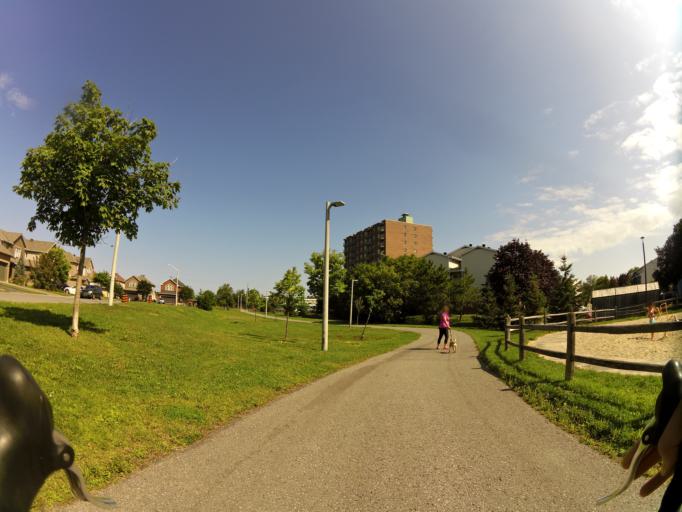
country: CA
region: Ontario
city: Ottawa
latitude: 45.3779
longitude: -75.6555
